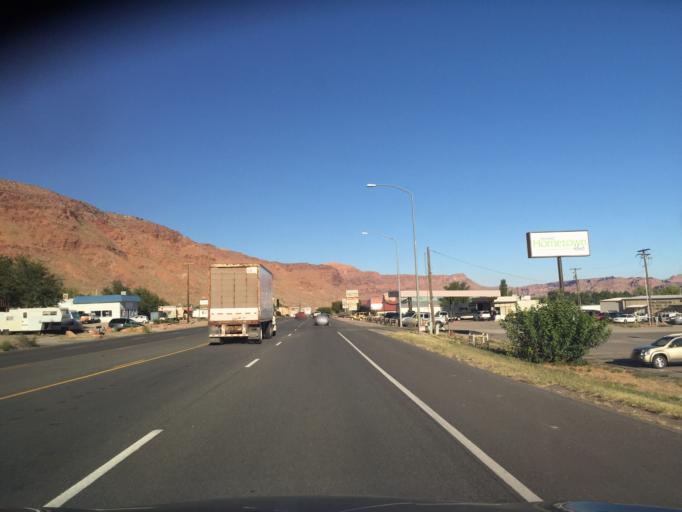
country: US
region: Utah
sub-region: Grand County
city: Moab
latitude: 38.5556
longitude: -109.5375
